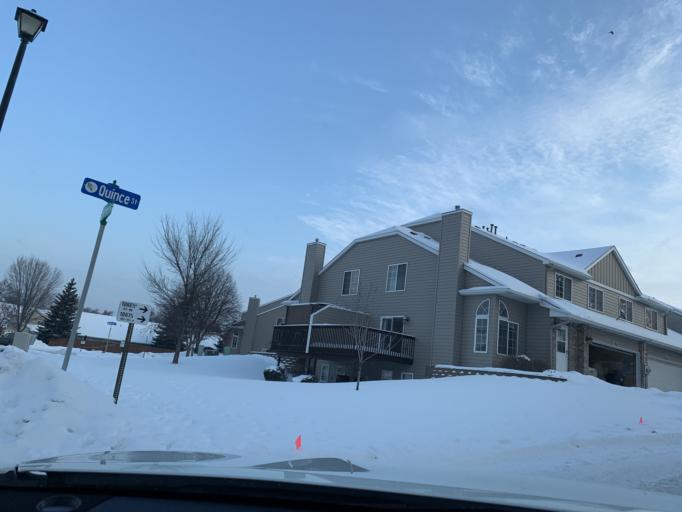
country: US
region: Minnesota
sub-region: Anoka County
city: Coon Rapids
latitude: 45.1635
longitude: -93.2890
